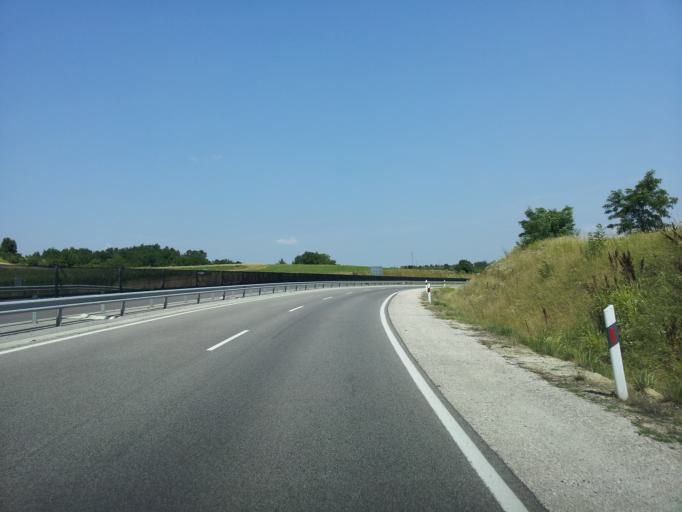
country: HU
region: Zala
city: Zalaegerszeg
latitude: 46.8362
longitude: 16.8852
